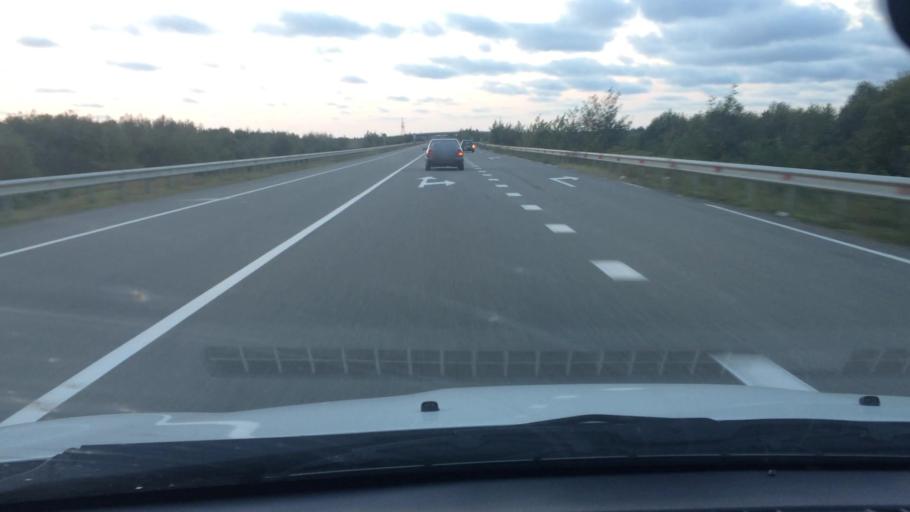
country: GE
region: Ajaria
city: Ochkhamuri
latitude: 41.8937
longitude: 41.8033
